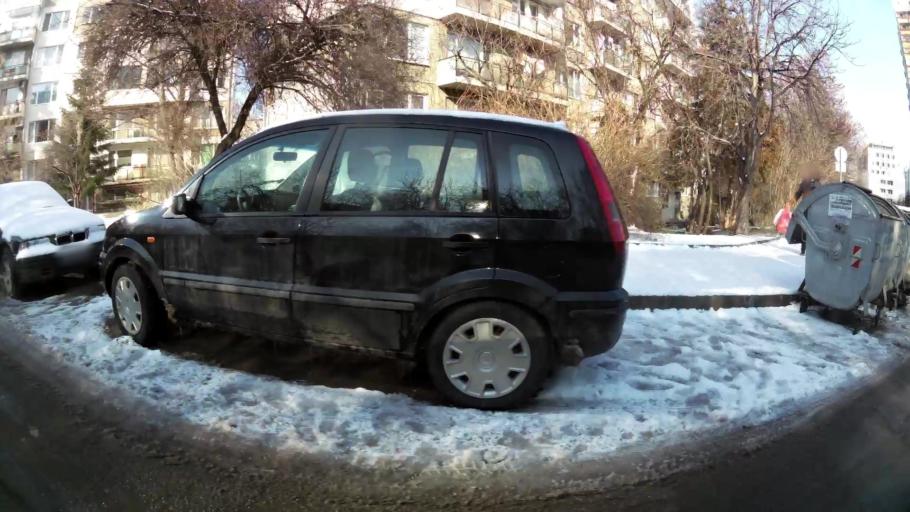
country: BG
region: Sofia-Capital
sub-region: Stolichna Obshtina
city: Sofia
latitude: 42.6618
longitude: 23.3502
